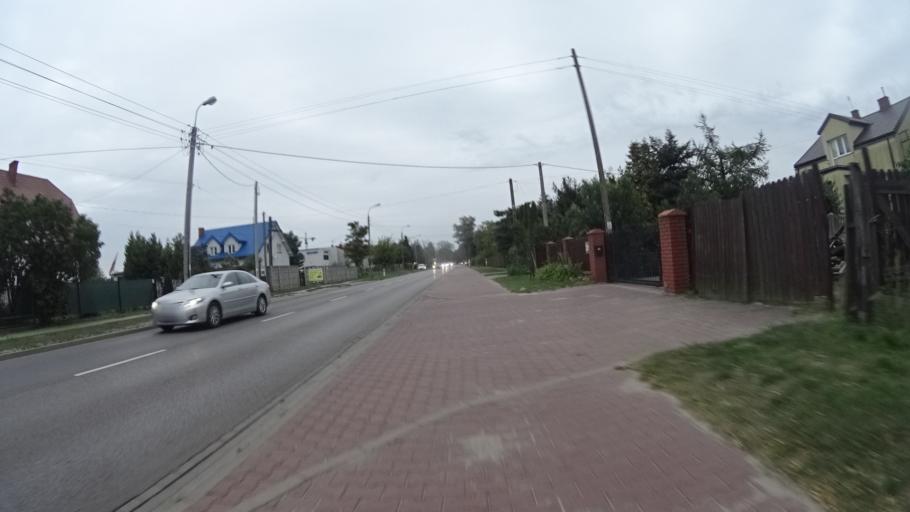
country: PL
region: Masovian Voivodeship
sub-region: Powiat warszawski zachodni
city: Stare Babice
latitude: 52.2527
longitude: 20.8110
